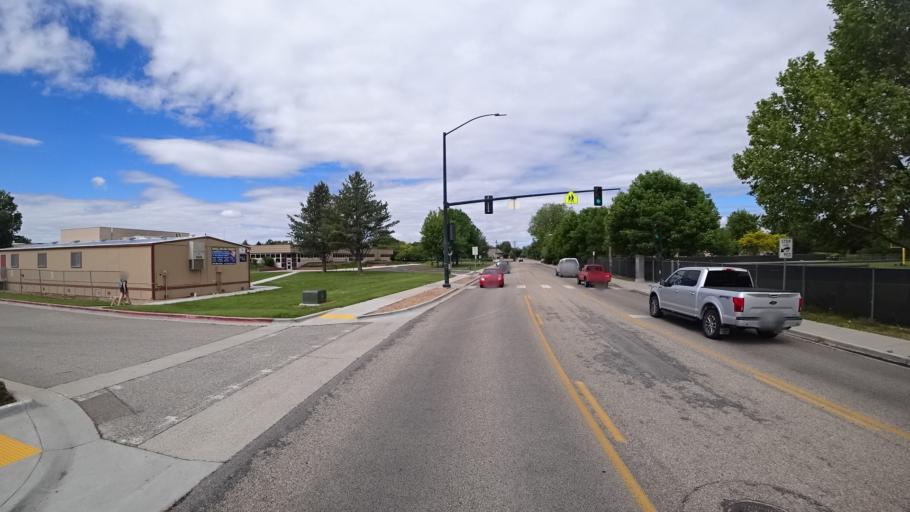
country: US
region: Idaho
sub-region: Ada County
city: Boise
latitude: 43.5787
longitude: -116.1773
